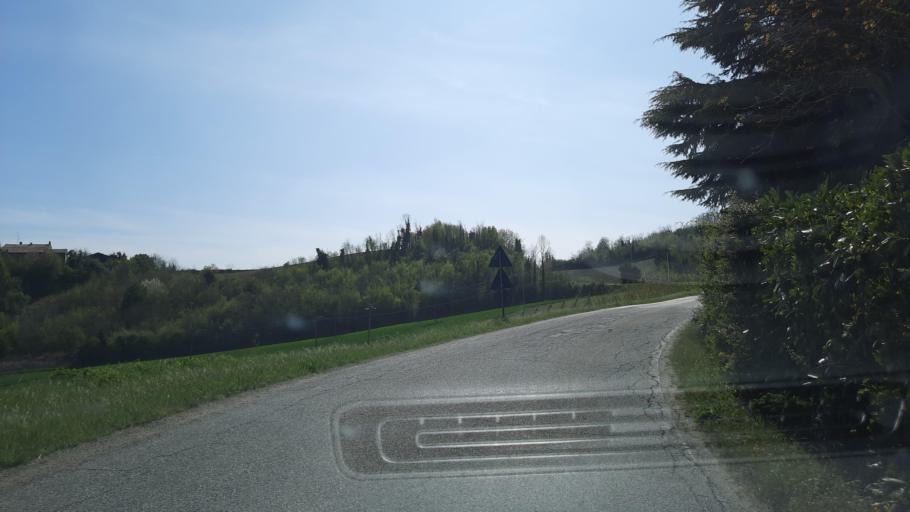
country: IT
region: Piedmont
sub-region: Provincia di Alessandria
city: Sala Monferrato
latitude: 45.0668
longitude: 8.3530
